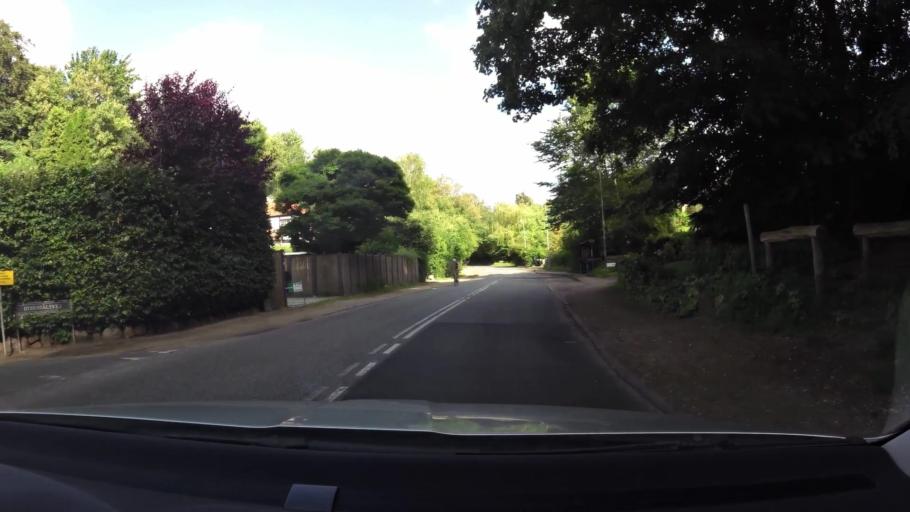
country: DK
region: Capital Region
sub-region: Rudersdal Kommune
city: Trorod
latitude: 55.7982
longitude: 12.5358
